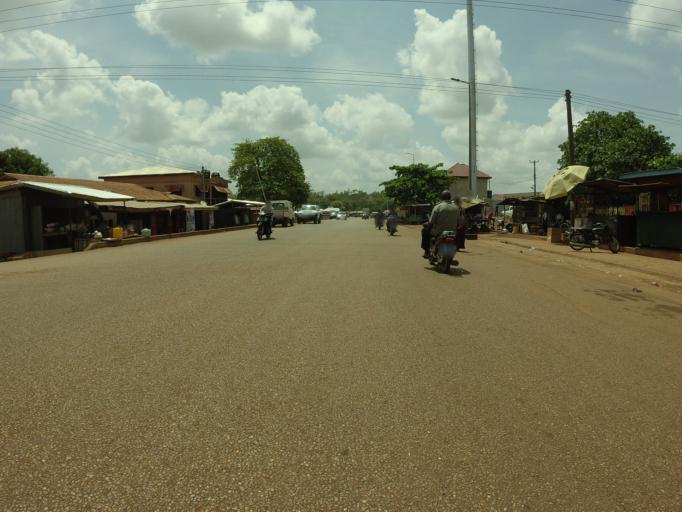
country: GH
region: Northern
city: Tamale
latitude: 9.4027
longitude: -0.8513
